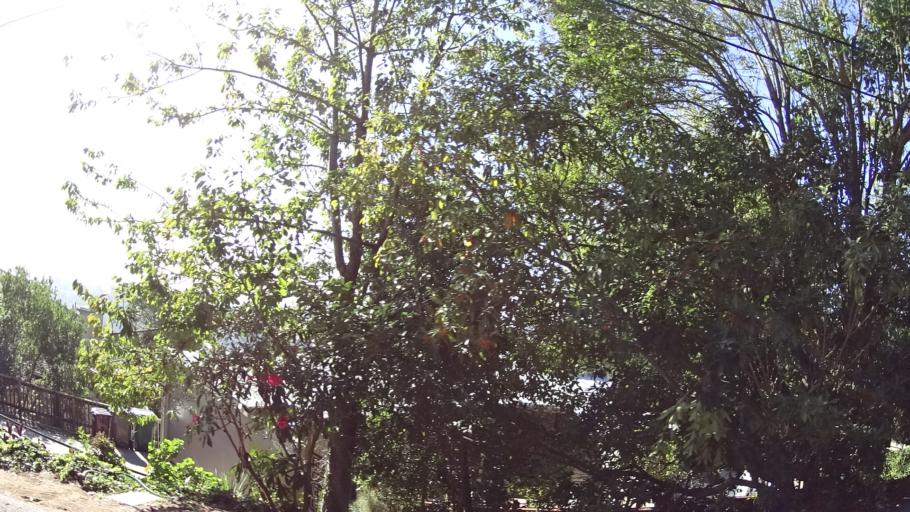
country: US
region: California
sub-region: Alameda County
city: Piedmont
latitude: 37.8292
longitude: -122.2052
